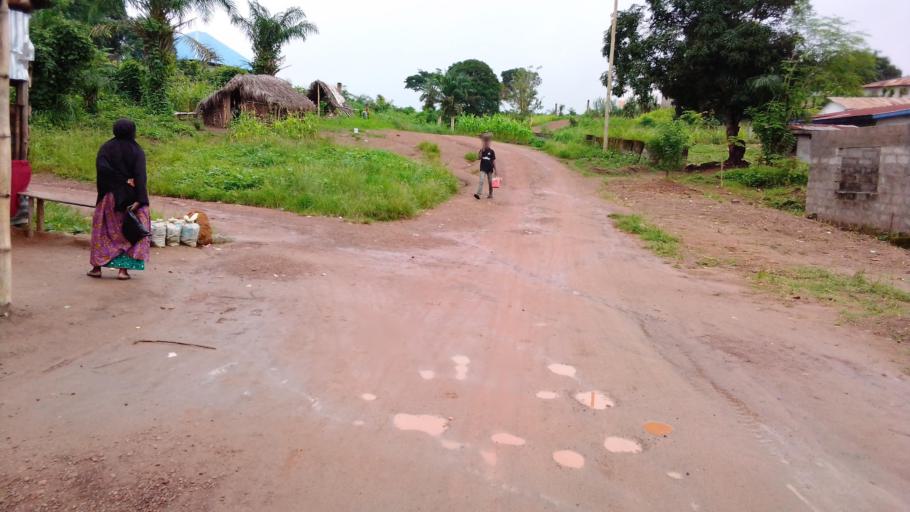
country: SL
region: Eastern Province
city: Kenema
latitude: 7.8634
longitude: -11.1730
